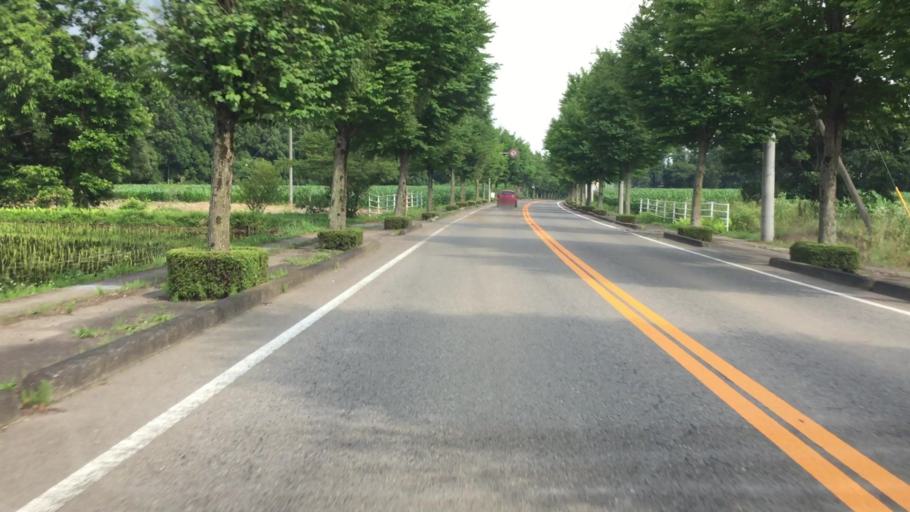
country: JP
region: Tochigi
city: Kuroiso
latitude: 36.9854
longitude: 139.9573
